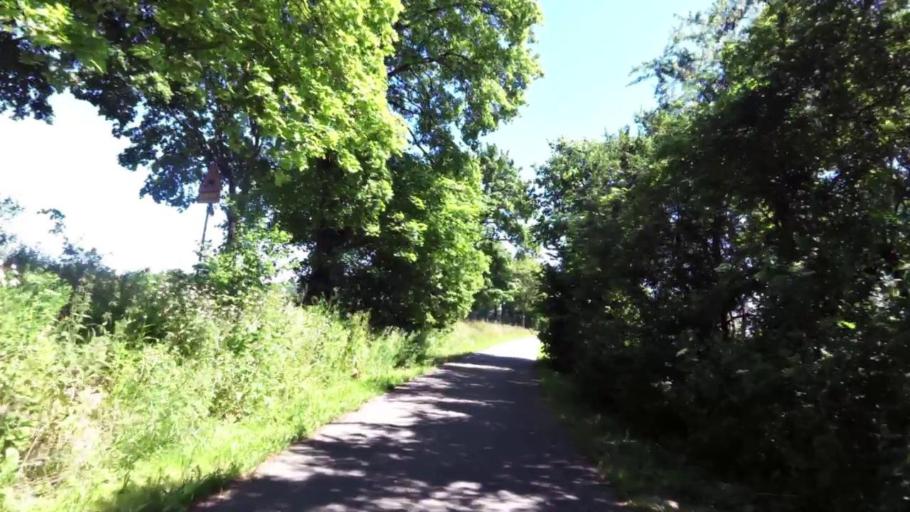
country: PL
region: West Pomeranian Voivodeship
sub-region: Powiat kolobrzeski
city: Goscino
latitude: 54.0365
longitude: 15.6733
